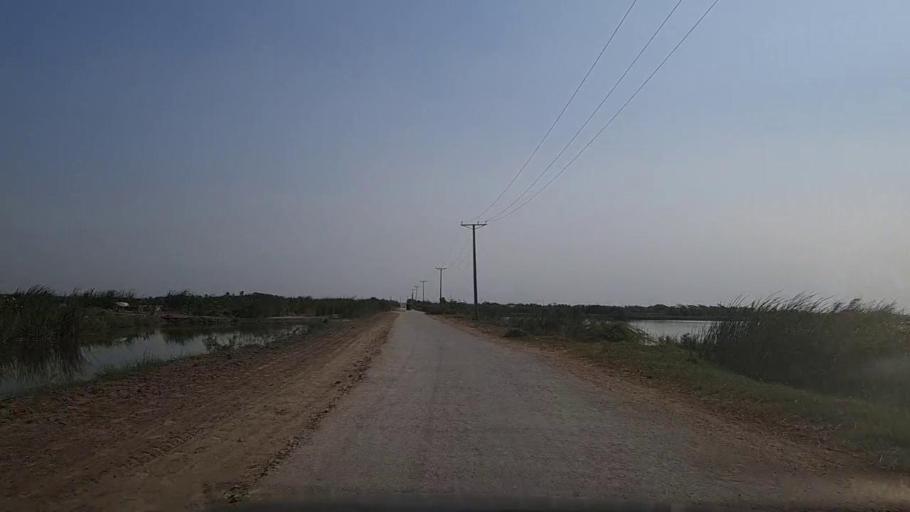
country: PK
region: Sindh
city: Thatta
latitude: 24.5840
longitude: 67.9094
